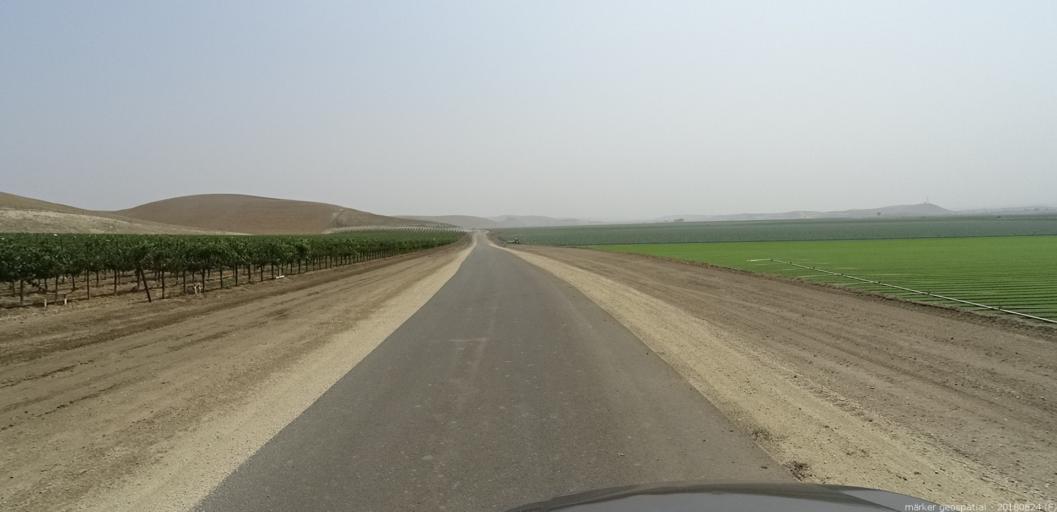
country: US
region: California
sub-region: Monterey County
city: King City
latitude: 36.1934
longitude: -121.0563
